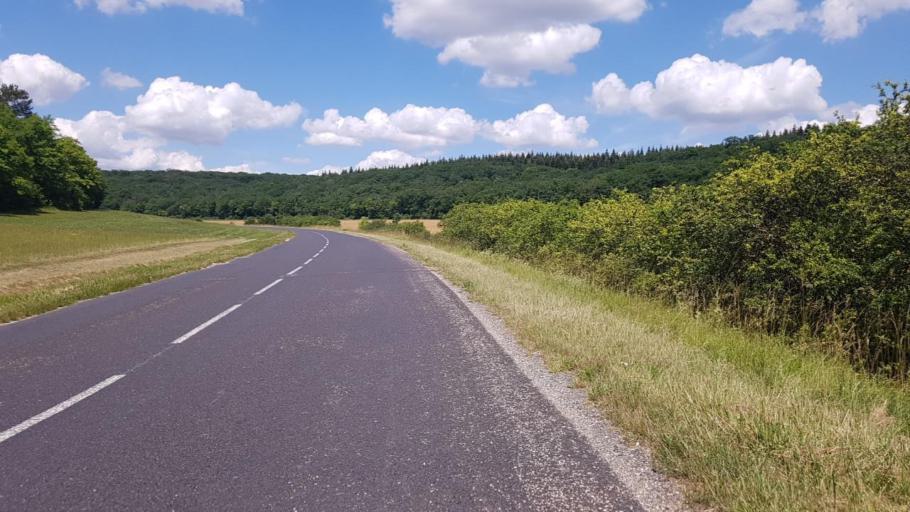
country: FR
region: Lorraine
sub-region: Departement de la Meuse
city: Vacon
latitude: 48.6712
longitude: 5.5977
